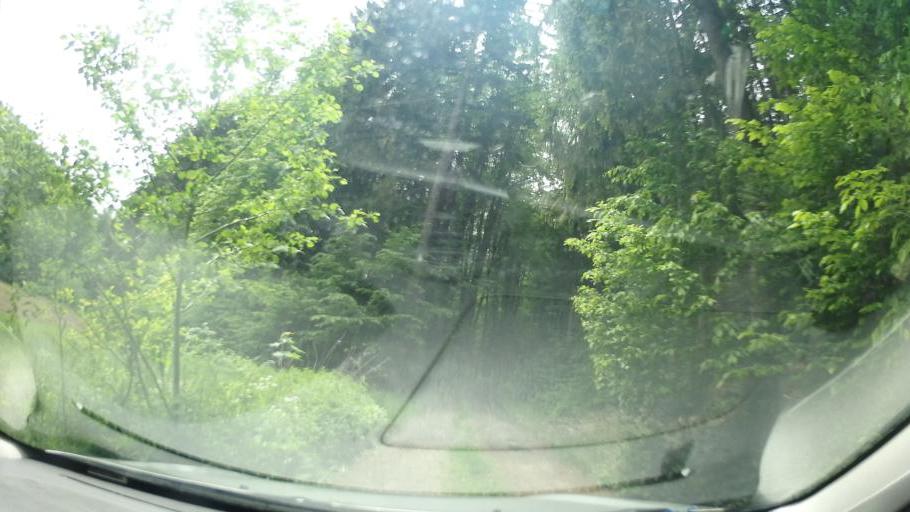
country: CZ
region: Olomoucky
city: Stity
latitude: 49.8720
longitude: 16.7391
